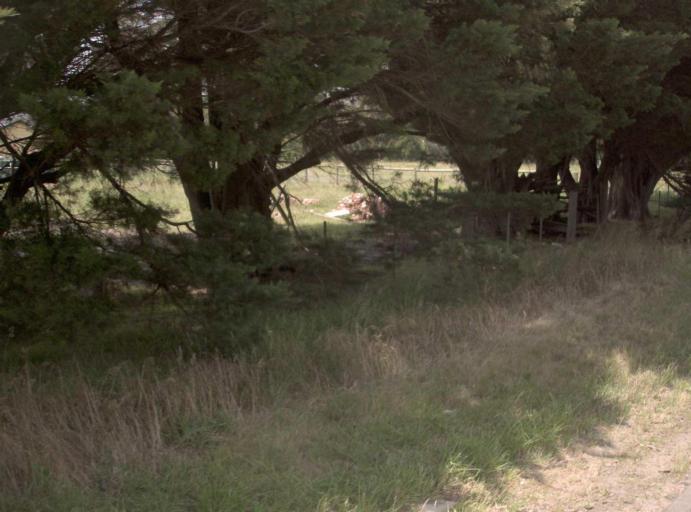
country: AU
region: Victoria
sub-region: Latrobe
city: Traralgon
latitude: -38.3759
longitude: 146.7544
